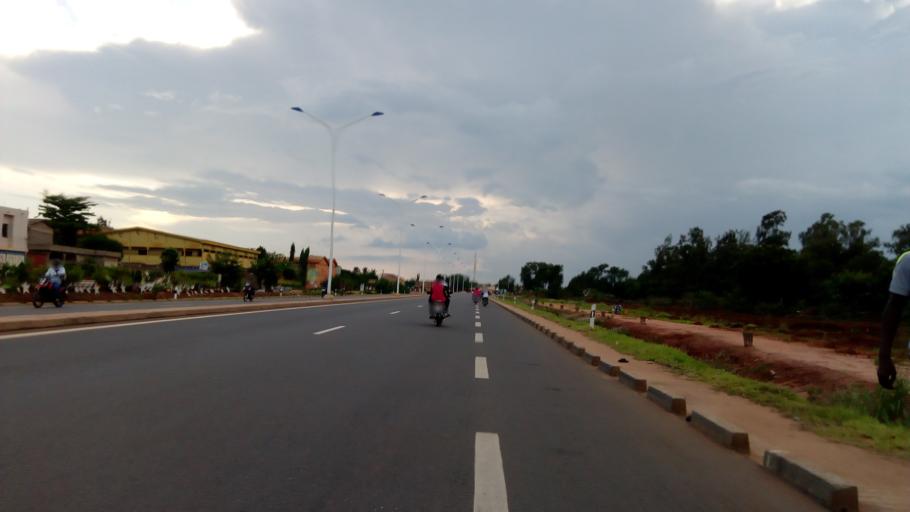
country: TG
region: Maritime
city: Lome
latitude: 6.2447
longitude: 1.1883
